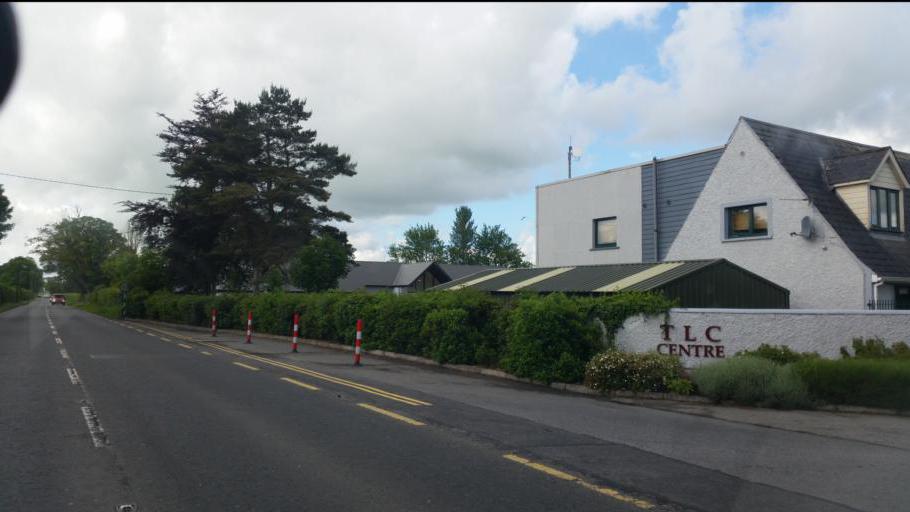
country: IE
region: Leinster
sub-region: Kildare
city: Maynooth
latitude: 53.3604
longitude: -6.5928
